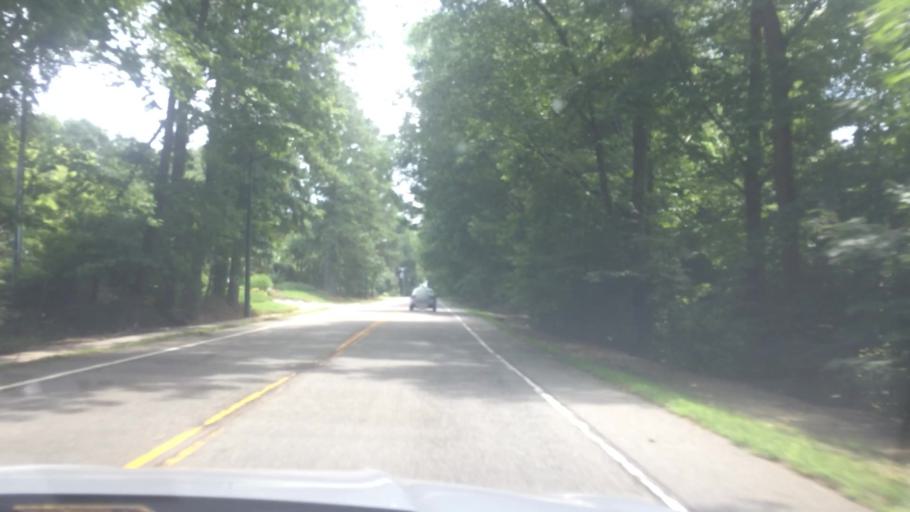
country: US
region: Virginia
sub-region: City of Williamsburg
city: Williamsburg
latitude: 37.2807
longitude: -76.6832
